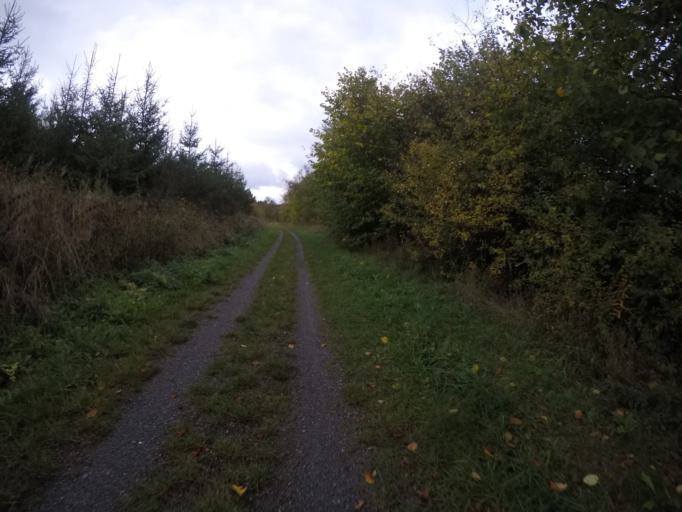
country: BE
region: Wallonia
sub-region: Province du Luxembourg
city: Fauvillers
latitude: 49.8504
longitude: 5.6973
